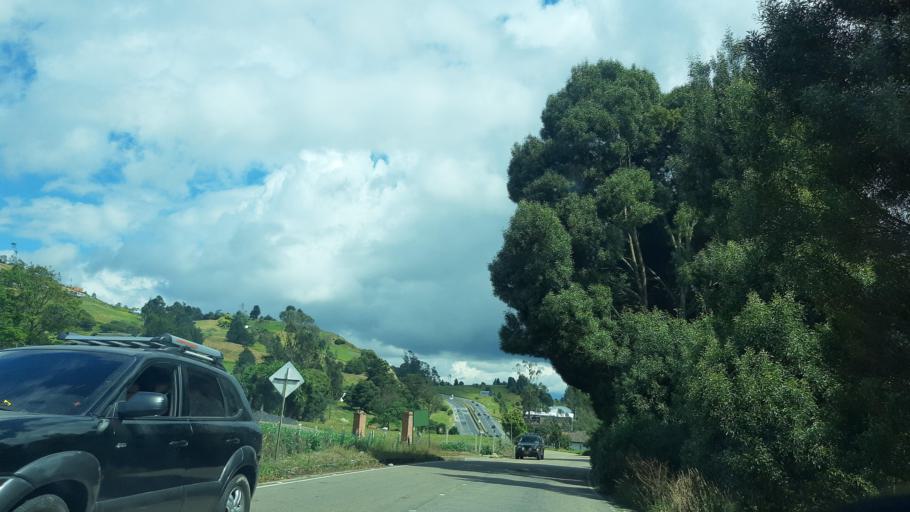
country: CO
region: Boyaca
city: Samaca
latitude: 5.4539
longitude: -73.4295
